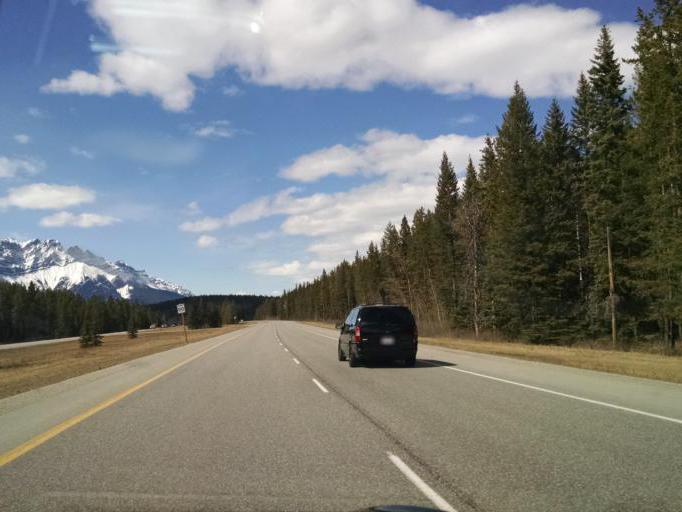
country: CA
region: Alberta
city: Canmore
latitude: 51.1528
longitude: -115.4320
